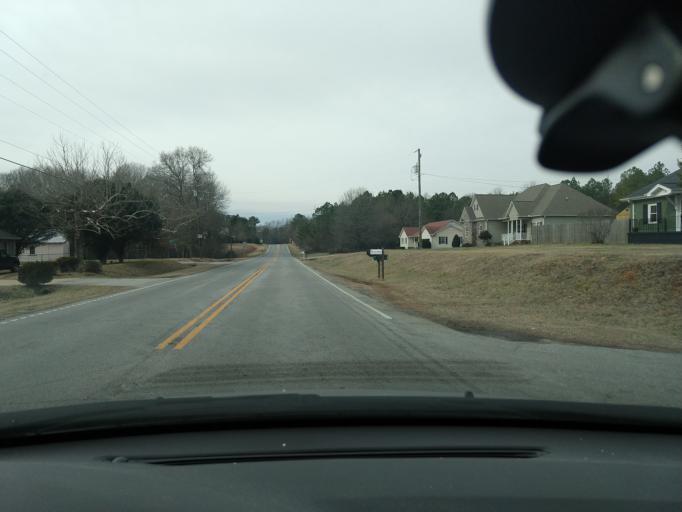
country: US
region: South Carolina
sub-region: Spartanburg County
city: Cowpens
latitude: 35.0097
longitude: -81.8652
